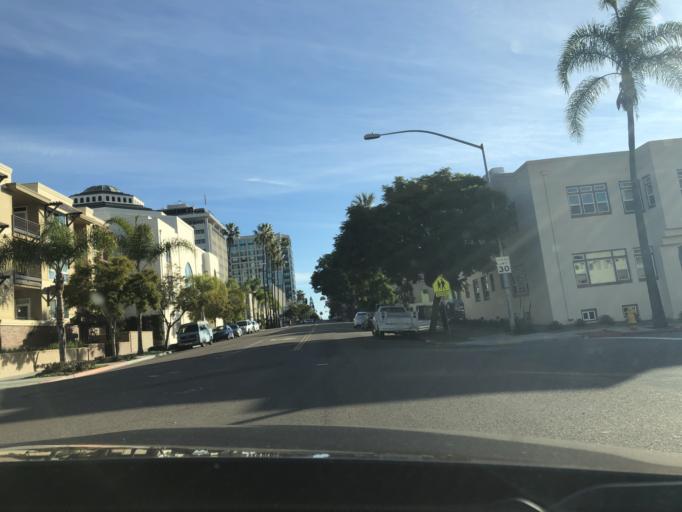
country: US
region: California
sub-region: San Diego County
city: San Diego
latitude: 32.7314
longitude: -117.1632
